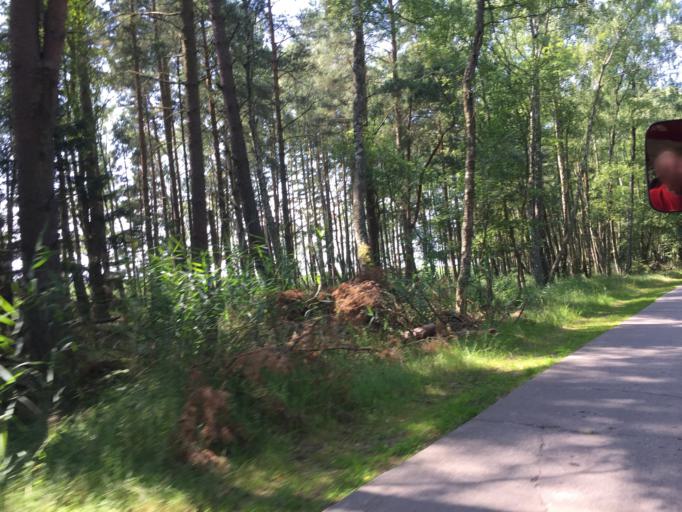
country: PL
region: Pomeranian Voivodeship
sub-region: Powiat leborski
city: Leba
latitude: 54.7529
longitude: 17.4934
